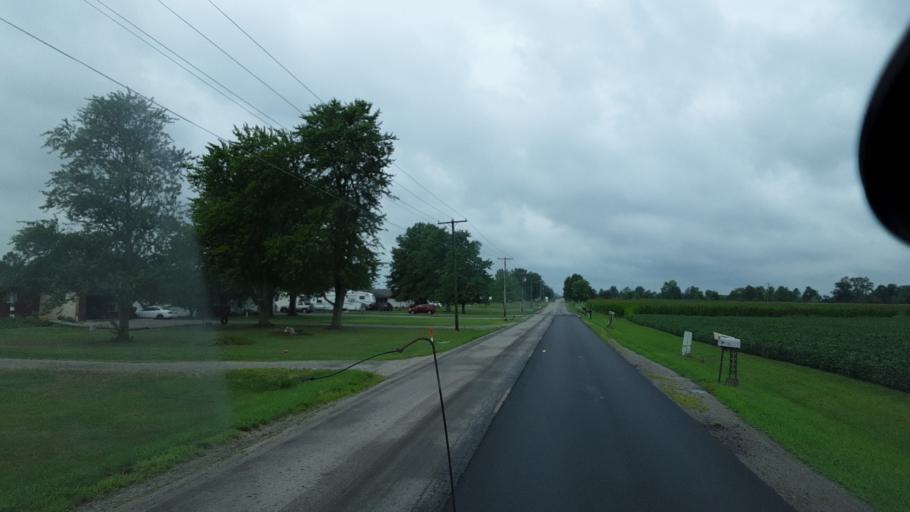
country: US
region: Indiana
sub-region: Allen County
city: New Haven
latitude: 40.9476
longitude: -85.0130
